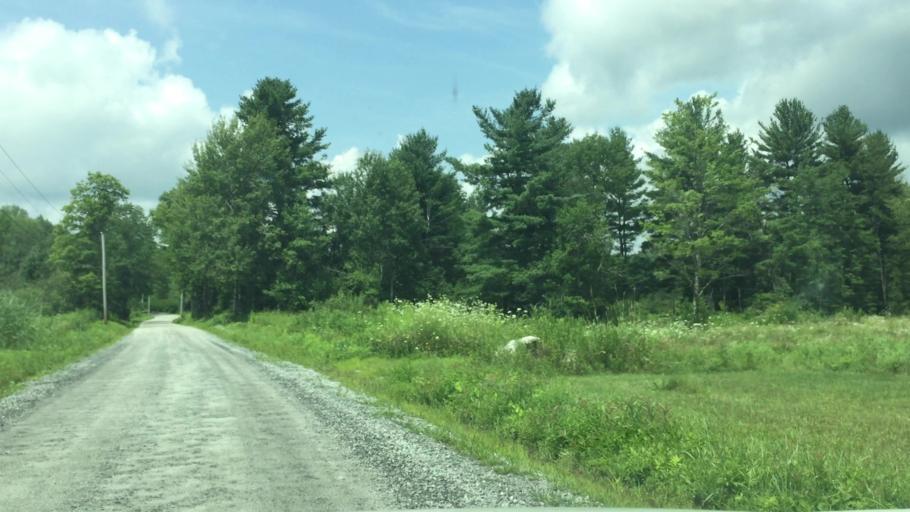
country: US
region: Massachusetts
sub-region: Berkshire County
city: Lee
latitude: 42.2719
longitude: -73.1746
